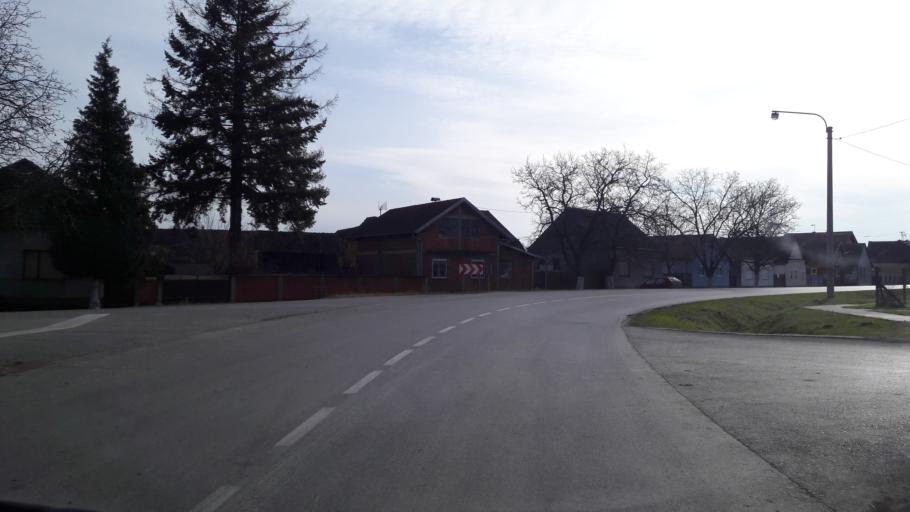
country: HR
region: Osjecko-Baranjska
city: Semeljci
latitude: 45.3514
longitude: 18.5573
